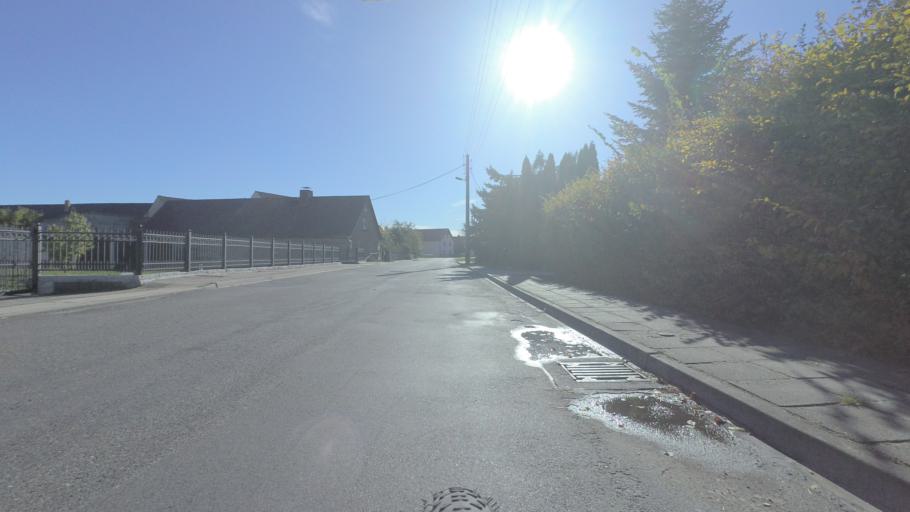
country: DE
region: Saxony
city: Nauwalde
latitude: 51.4421
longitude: 13.4506
